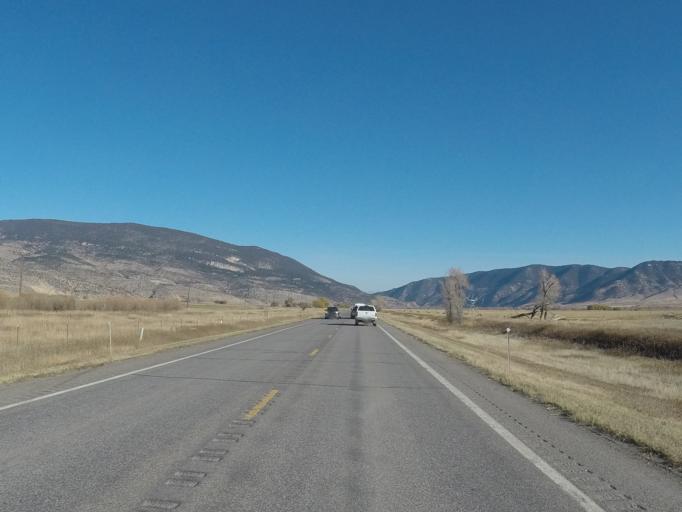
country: US
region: Montana
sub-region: Park County
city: Livingston
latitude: 45.5352
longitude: -110.6035
